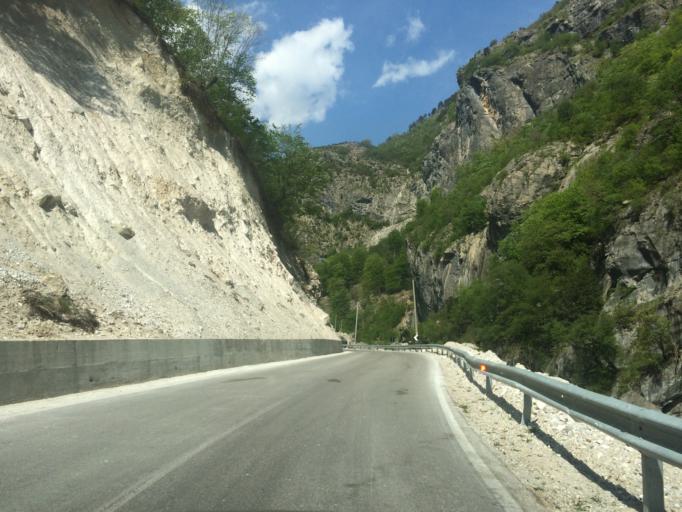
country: AL
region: Kukes
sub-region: Rrethi i Tropojes
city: Bajram Curri
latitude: 42.4147
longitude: 20.0160
